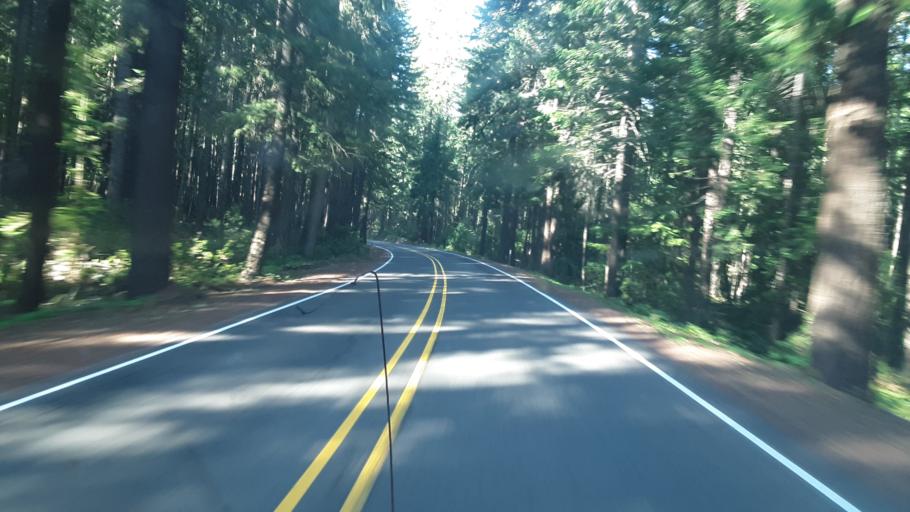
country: US
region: Oregon
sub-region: Jackson County
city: Shady Cove
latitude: 42.9417
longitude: -122.4180
